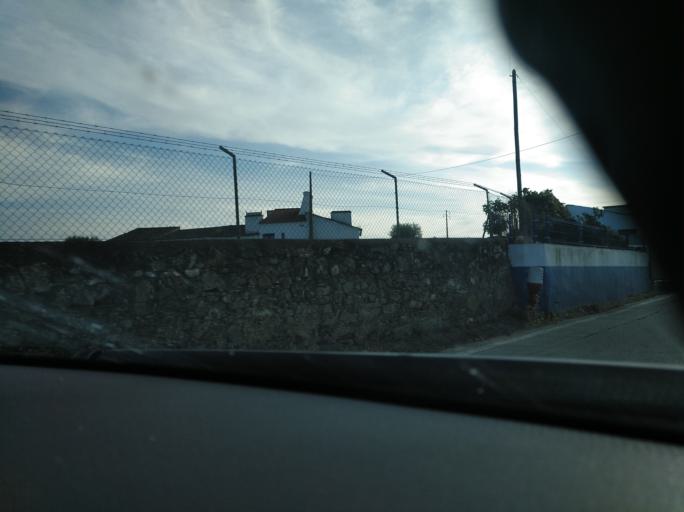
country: PT
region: Portalegre
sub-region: Fronteira
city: Fronteira
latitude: 38.9560
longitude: -7.6648
